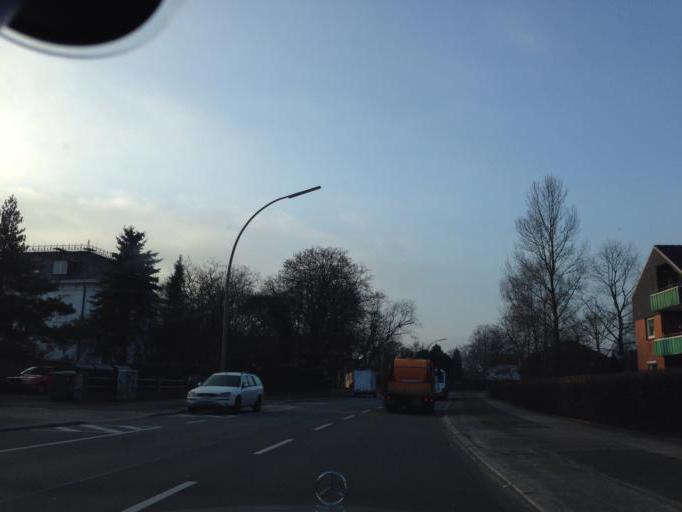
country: DE
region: Schleswig-Holstein
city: Barsbuettel
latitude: 53.6047
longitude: 10.1731
